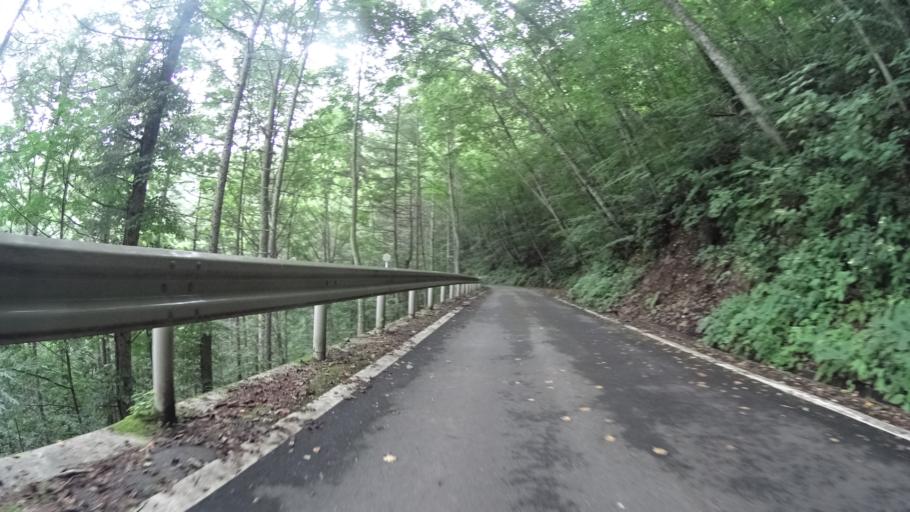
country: JP
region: Yamanashi
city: Kofu-shi
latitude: 35.8080
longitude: 138.6209
